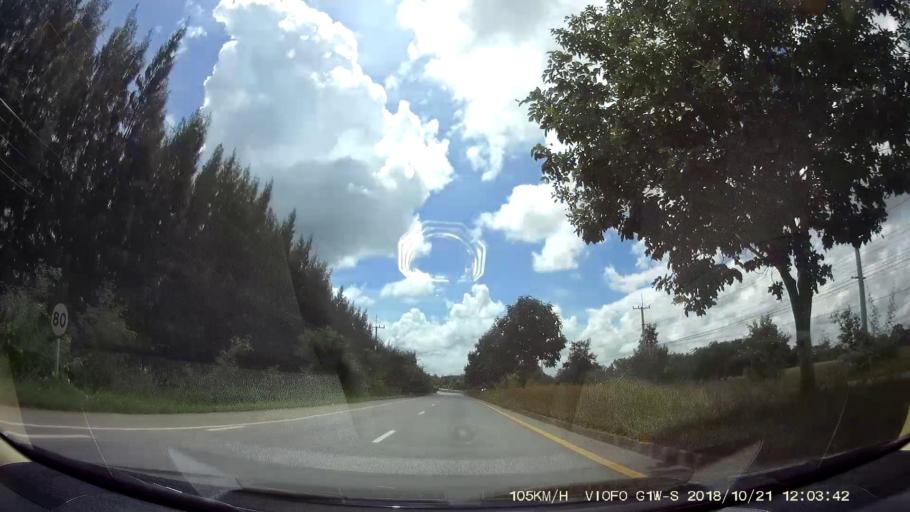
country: TH
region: Chaiyaphum
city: Chatturat
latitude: 15.5052
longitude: 101.8208
